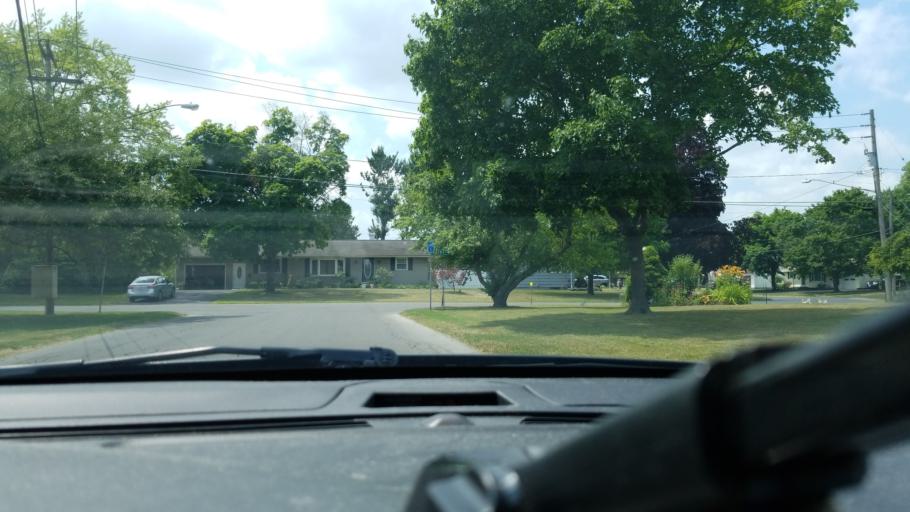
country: US
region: New York
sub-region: Onondaga County
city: Galeville
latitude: 43.1072
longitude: -76.1769
